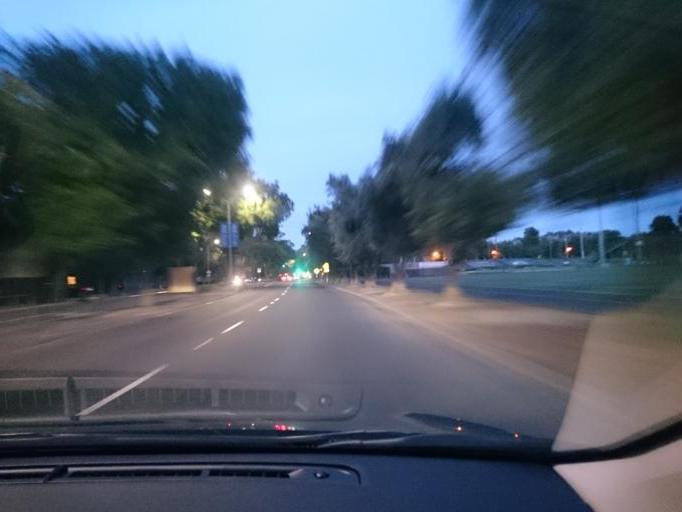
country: US
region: California
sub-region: Yolo County
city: Davis
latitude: 38.5461
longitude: -121.7500
